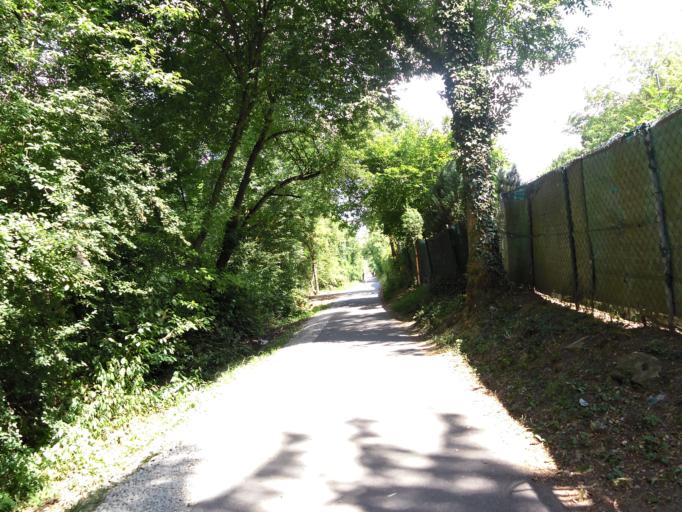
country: DE
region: Bavaria
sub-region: Regierungsbezirk Unterfranken
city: Randersacker
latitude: 49.7636
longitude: 9.9580
